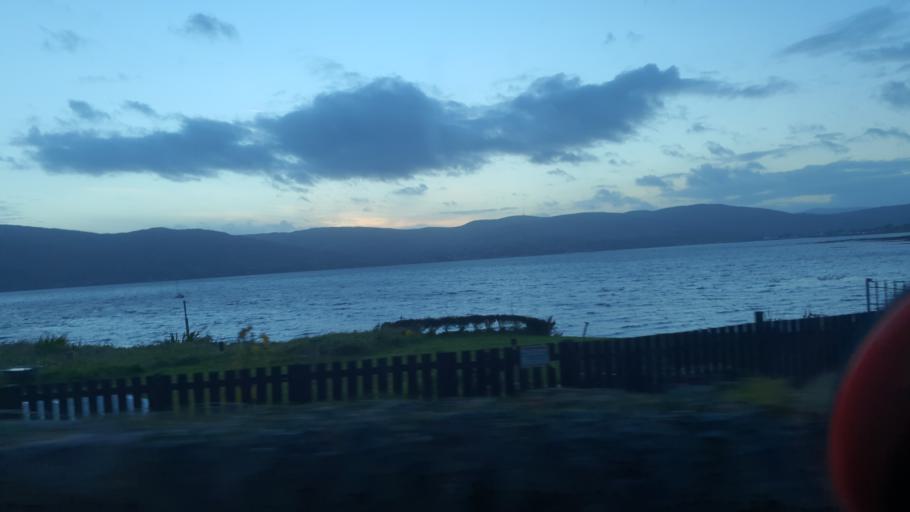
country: GB
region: Northern Ireland
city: Rostrevor
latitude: 54.0929
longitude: -6.1898
